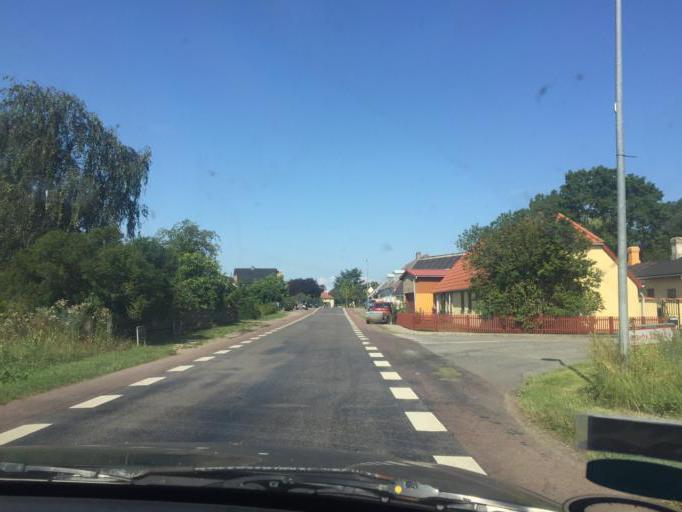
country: DK
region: Zealand
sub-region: Lolland Kommune
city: Maribo
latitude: 54.7965
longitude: 11.5265
